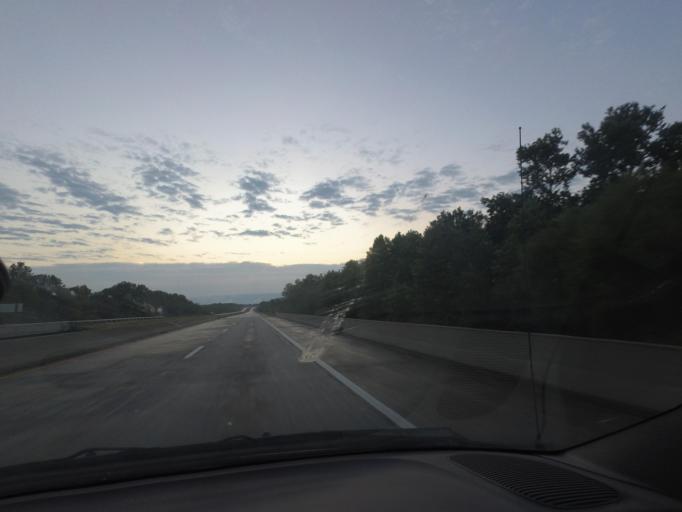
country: US
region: Missouri
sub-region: Macon County
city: Macon
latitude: 39.7587
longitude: -92.5975
